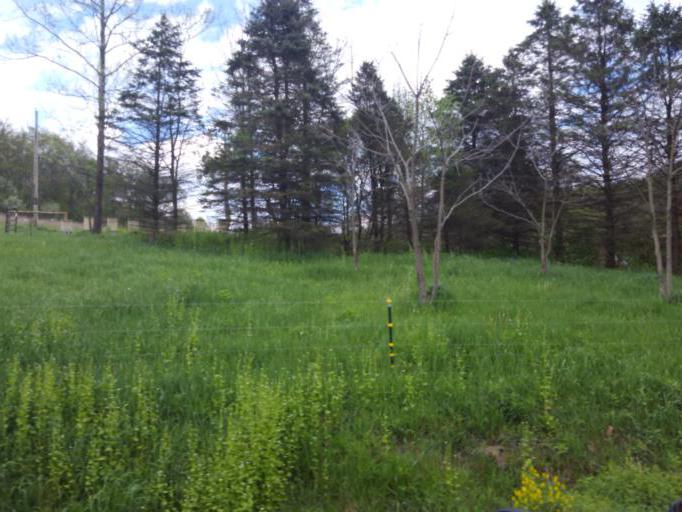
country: US
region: Ohio
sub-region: Ashland County
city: Loudonville
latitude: 40.5413
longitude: -82.2298
